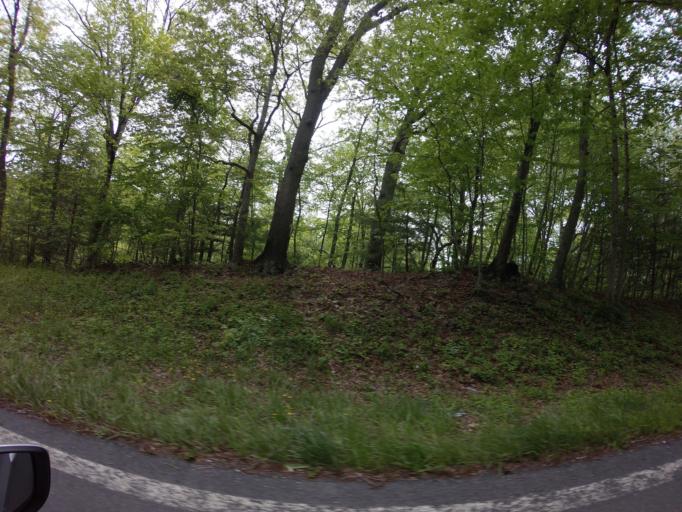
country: US
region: Maryland
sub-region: Carroll County
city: Eldersburg
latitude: 39.4548
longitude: -76.9563
